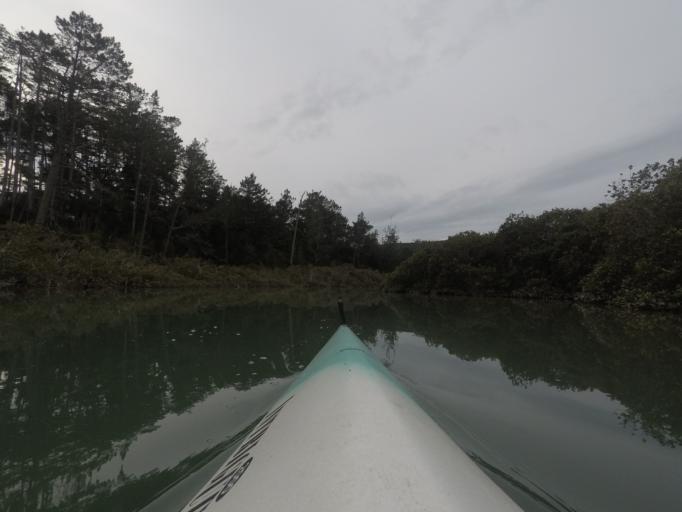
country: NZ
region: Auckland
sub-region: Auckland
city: Rothesay Bay
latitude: -36.6779
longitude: 174.7081
